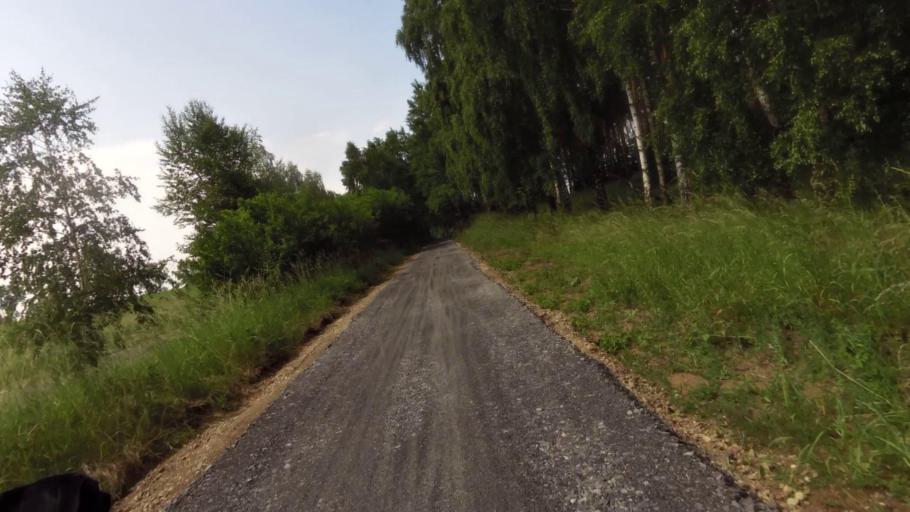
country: PL
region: West Pomeranian Voivodeship
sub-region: Powiat pyrzycki
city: Bielice
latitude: 53.2060
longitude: 14.6154
